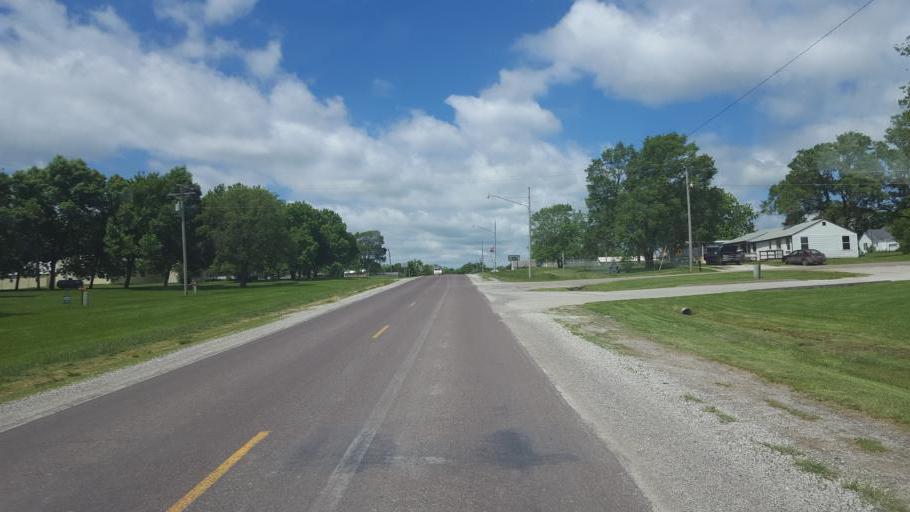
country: US
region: Iowa
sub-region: Decatur County
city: Lamoni
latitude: 40.4675
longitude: -93.9849
